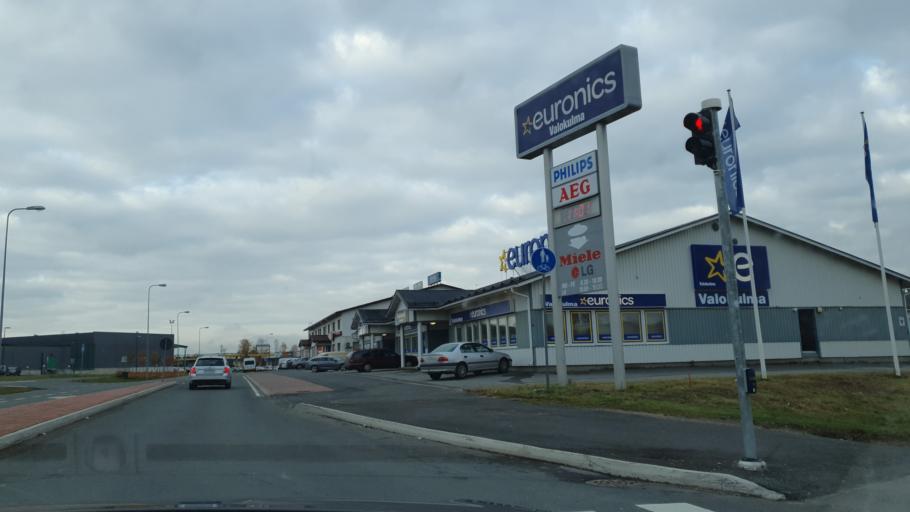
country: FI
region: Lapland
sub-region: Rovaniemi
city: Rovaniemi
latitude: 66.4934
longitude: 25.6913
